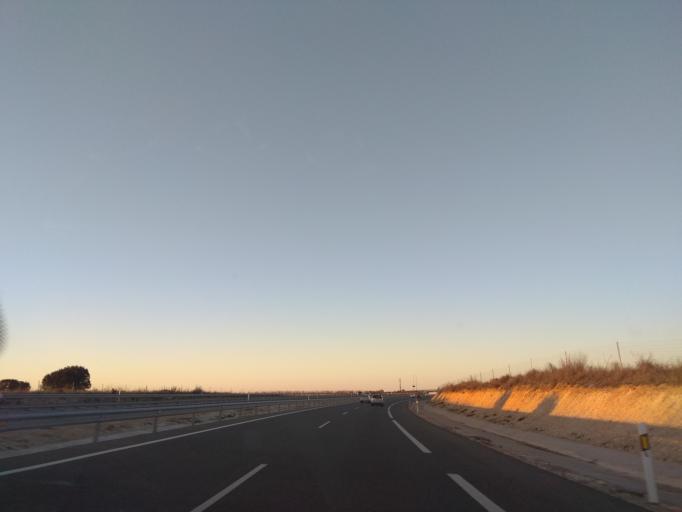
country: ES
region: Castille and Leon
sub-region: Provincia de Burgos
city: Aranda de Duero
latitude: 41.7322
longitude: -3.6883
